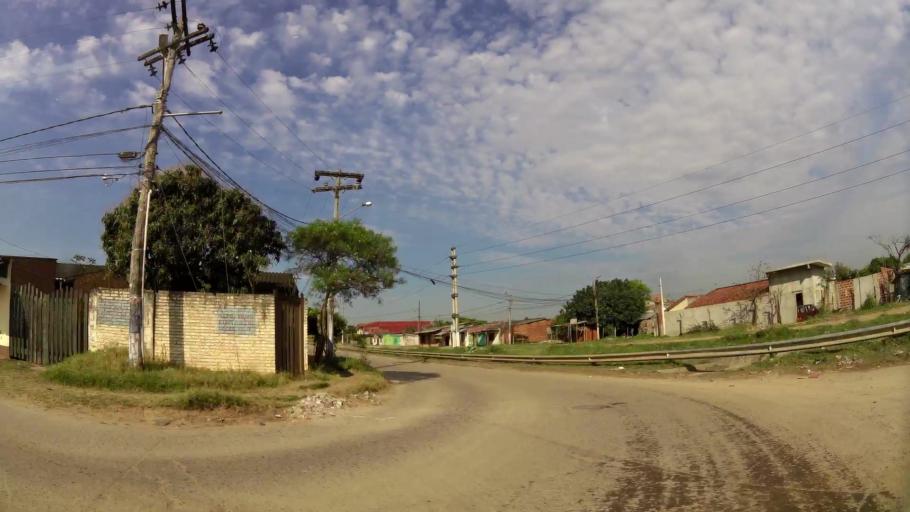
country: BO
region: Santa Cruz
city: Santa Cruz de la Sierra
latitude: -17.7295
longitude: -63.1758
